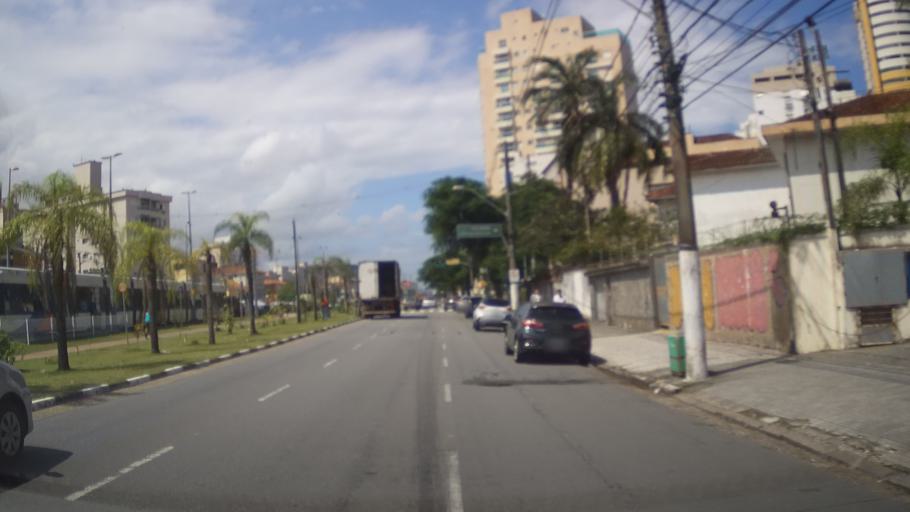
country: BR
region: Sao Paulo
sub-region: Santos
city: Santos
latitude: -23.9628
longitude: -46.3415
